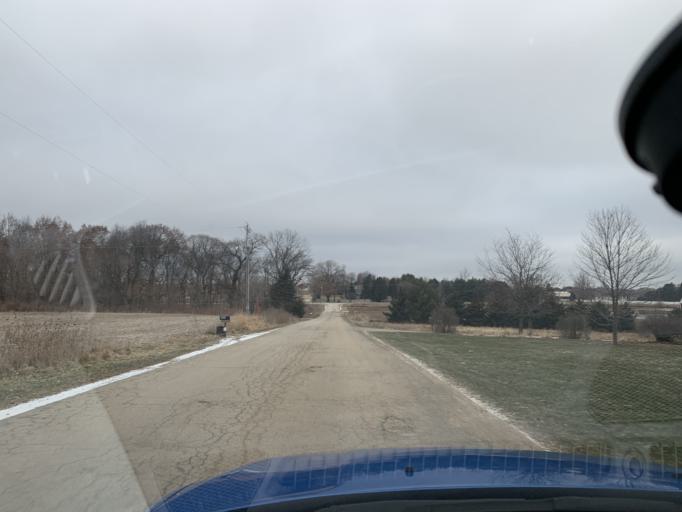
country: US
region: Wisconsin
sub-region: Dane County
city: Middleton
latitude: 43.0721
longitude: -89.5633
